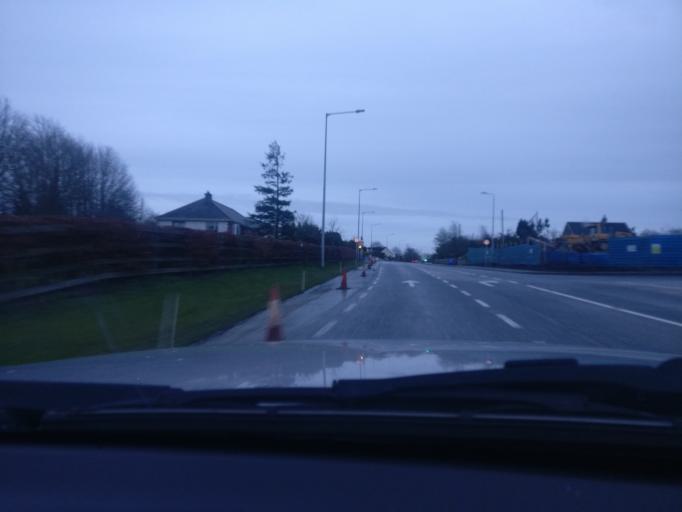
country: IE
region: Leinster
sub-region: An Mhi
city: Kells
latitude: 53.7318
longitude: -6.8895
